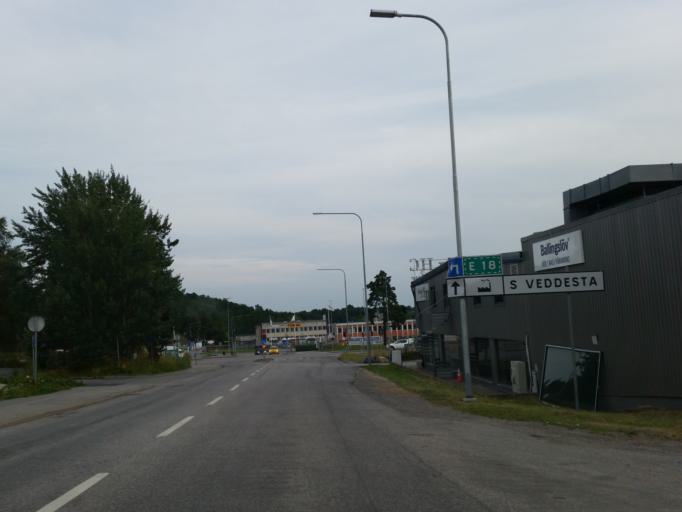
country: SE
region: Stockholm
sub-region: Jarfalla Kommun
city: Jakobsberg
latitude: 59.4081
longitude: 17.8407
